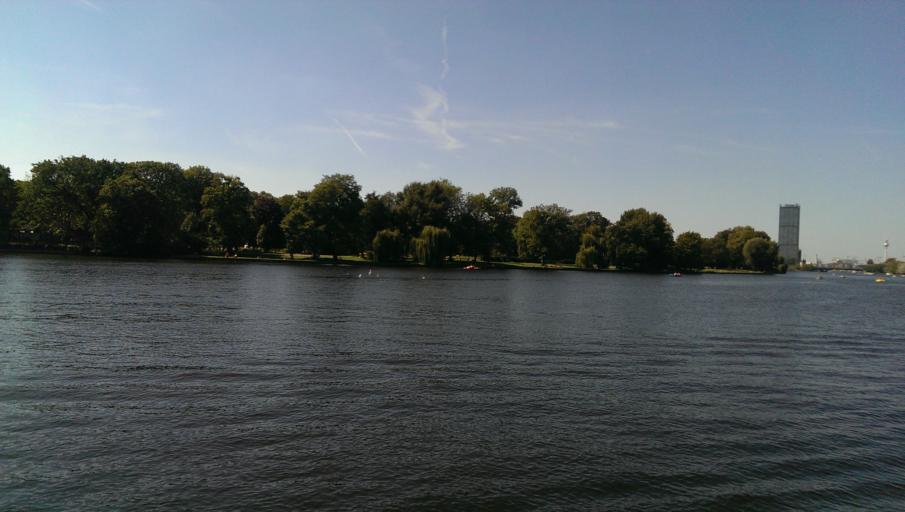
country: DE
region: Berlin
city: Plaenterwald
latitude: 52.4888
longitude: 13.4800
